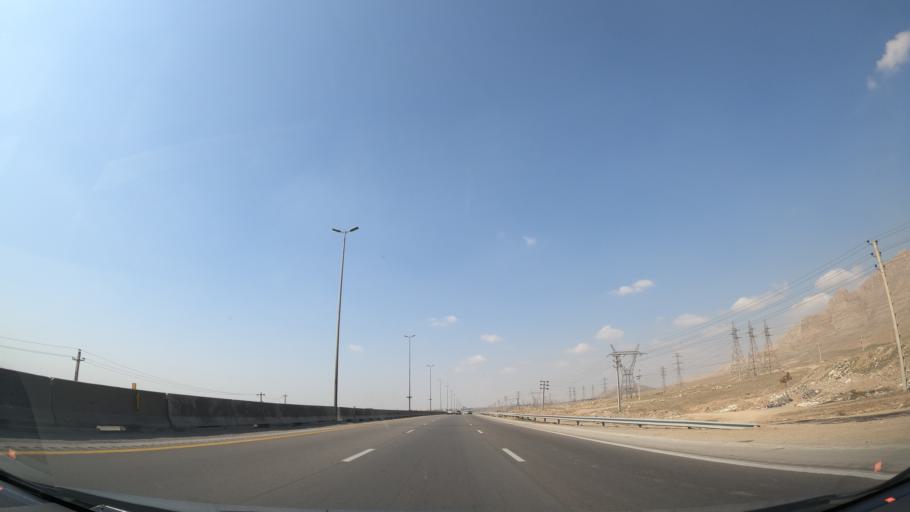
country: IR
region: Qazvin
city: Abyek
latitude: 36.0535
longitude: 50.5121
